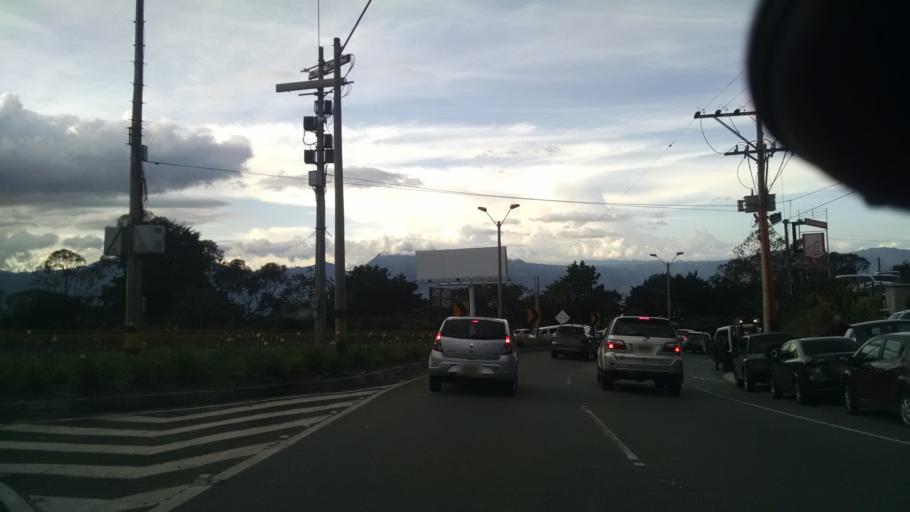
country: CO
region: Antioquia
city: Envigado
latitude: 6.1717
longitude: -75.5466
